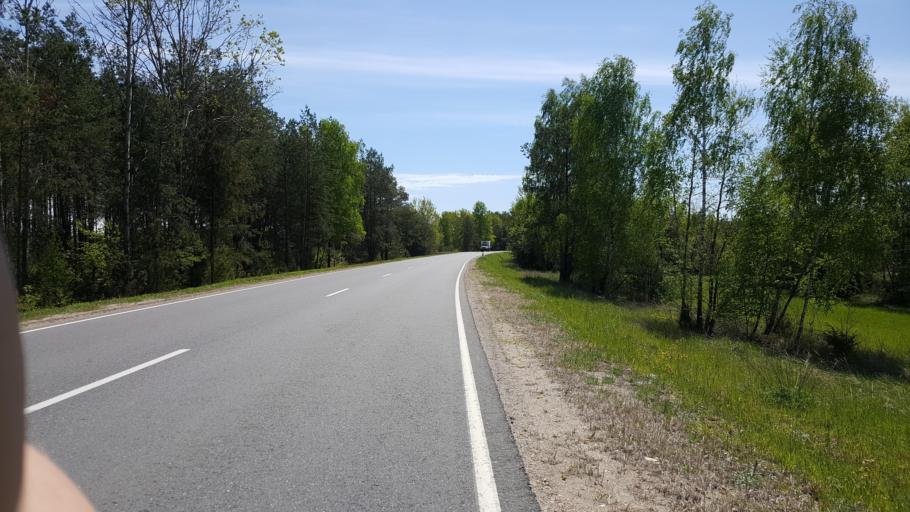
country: BY
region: Brest
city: Zhabinka
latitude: 52.3731
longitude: 24.1362
